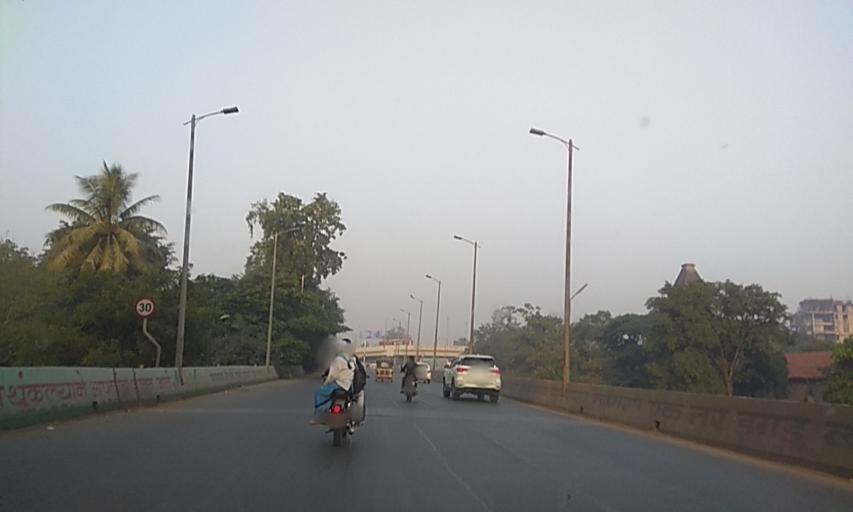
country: IN
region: Maharashtra
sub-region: Pune Division
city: Shivaji Nagar
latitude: 18.5298
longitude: 73.8569
